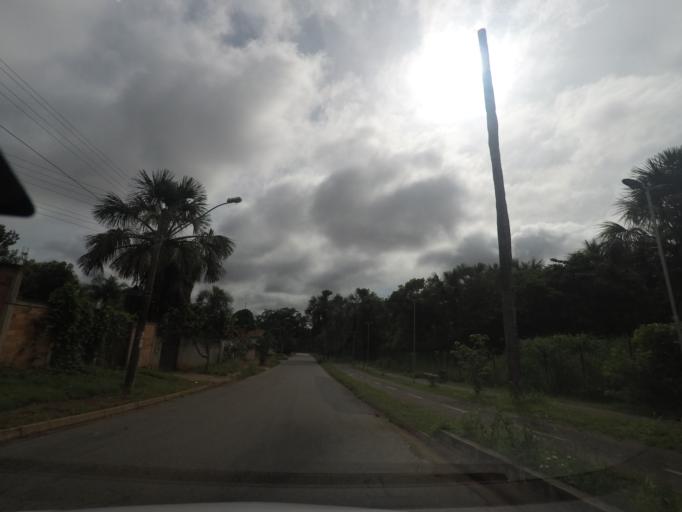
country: BR
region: Goias
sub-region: Goiania
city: Goiania
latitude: -16.7403
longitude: -49.3229
